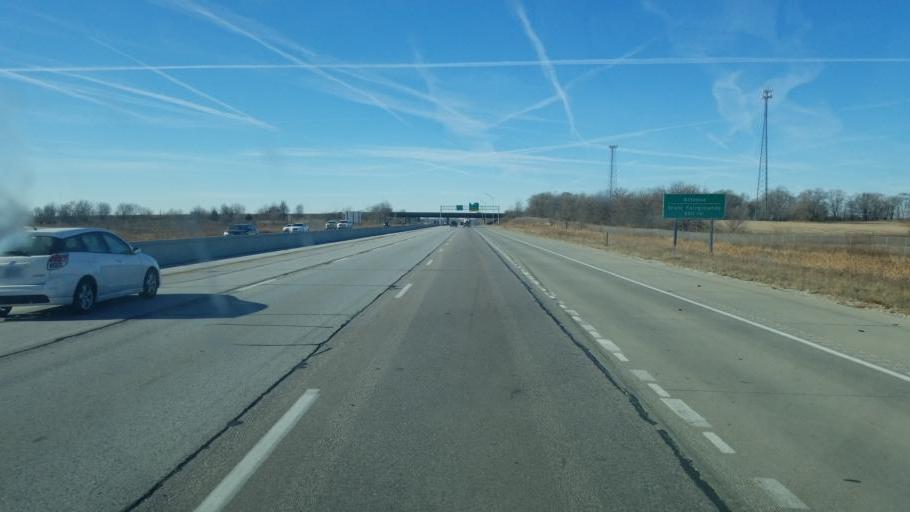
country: US
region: Iowa
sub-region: Polk County
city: Altoona
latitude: 41.6610
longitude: -93.5157
